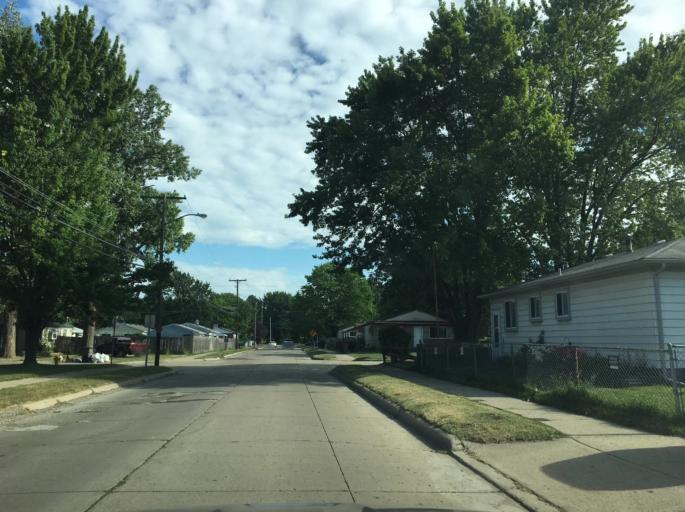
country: US
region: Michigan
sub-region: Macomb County
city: Clinton
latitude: 42.5527
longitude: -82.9102
